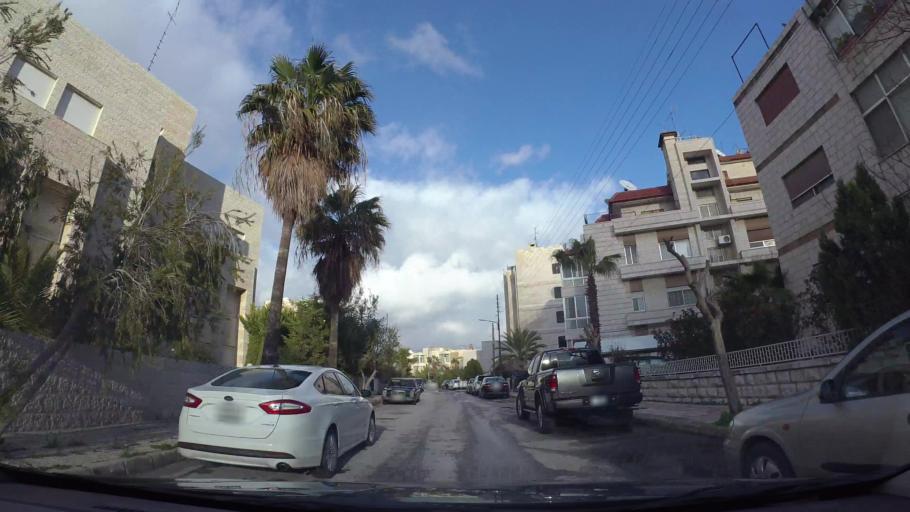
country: JO
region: Amman
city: Amman
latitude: 31.9541
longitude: 35.8941
